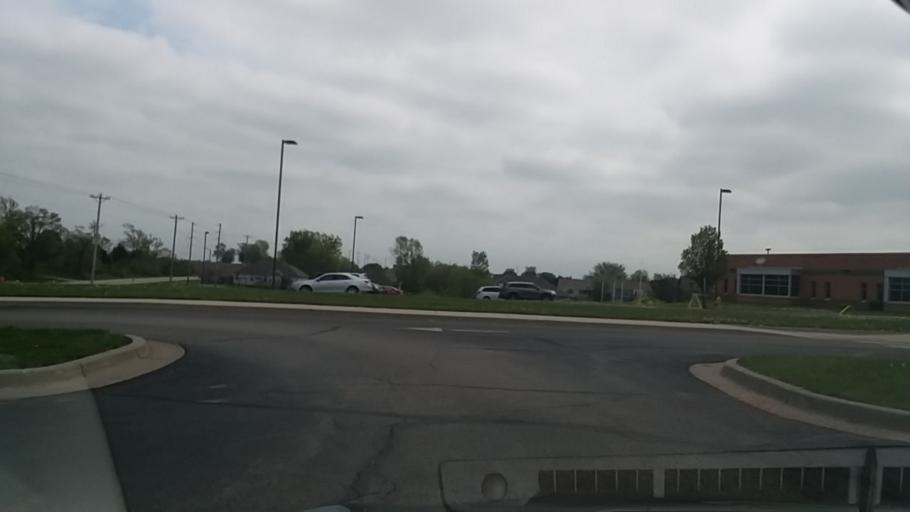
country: US
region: Kansas
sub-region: Douglas County
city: Eudora
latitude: 38.9417
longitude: -95.0874
